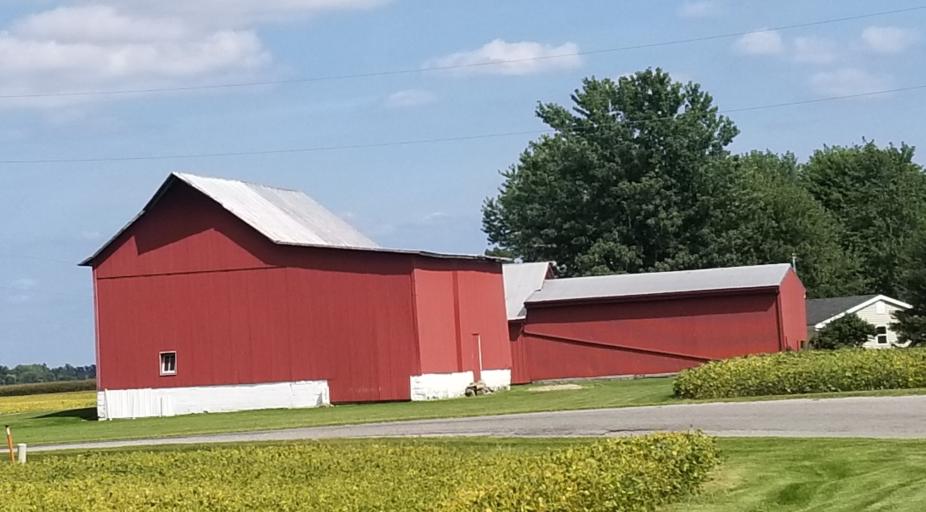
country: US
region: Ohio
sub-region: Union County
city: Richwood
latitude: 40.3973
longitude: -83.4449
